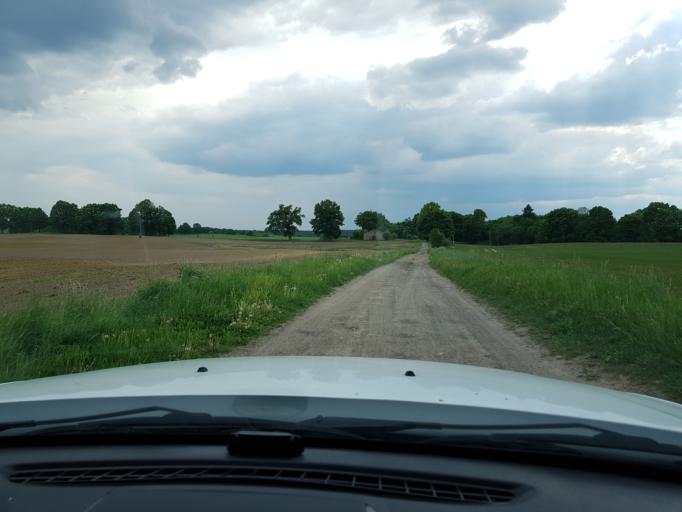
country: PL
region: West Pomeranian Voivodeship
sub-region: Powiat drawski
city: Drawsko Pomorskie
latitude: 53.5390
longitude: 15.7346
